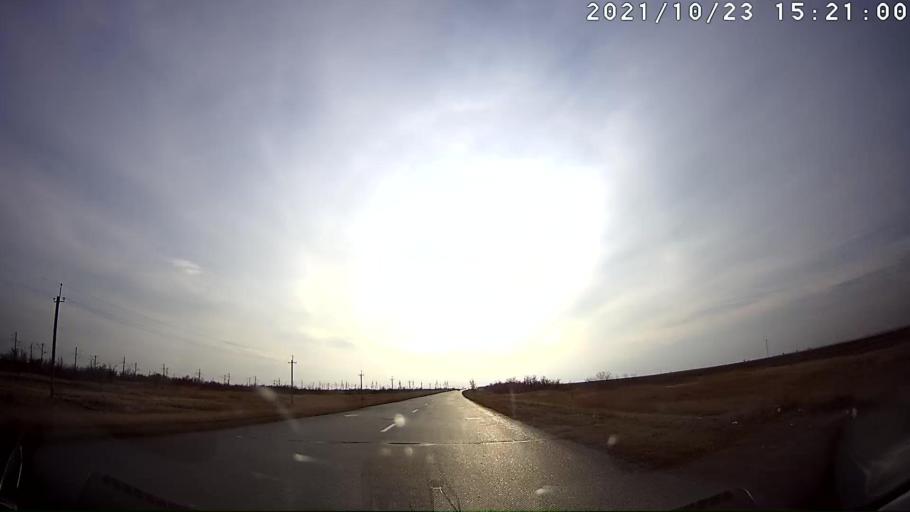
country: RU
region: Volgograd
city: Bereslavka
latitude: 48.3157
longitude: 44.3192
